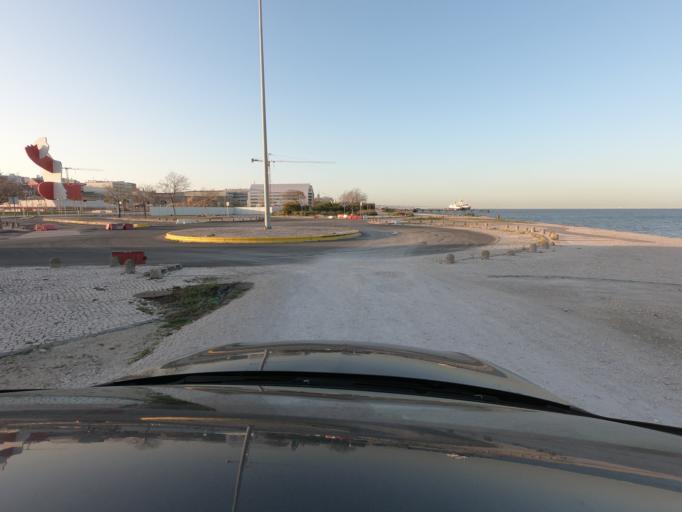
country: PT
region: Lisbon
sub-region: Loures
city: Moscavide
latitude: 38.7424
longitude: -9.0979
